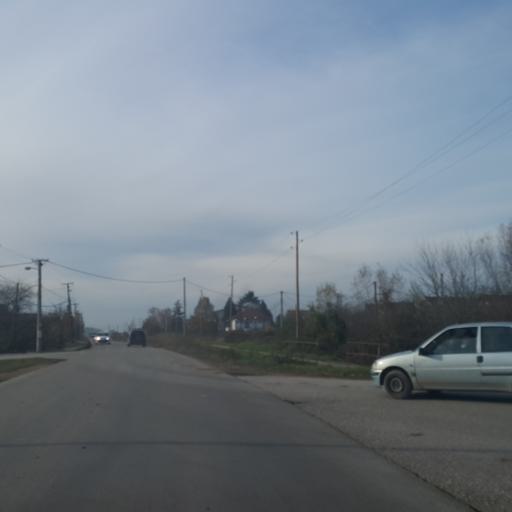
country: RS
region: Central Serbia
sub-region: Belgrade
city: Lazarevac
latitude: 44.3980
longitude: 20.3747
